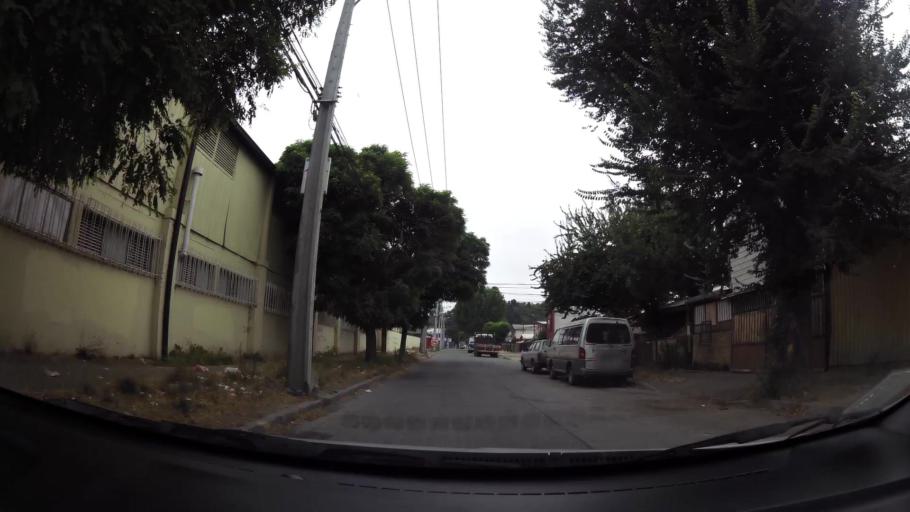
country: CL
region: Biobio
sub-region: Provincia de Concepcion
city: Concepcion
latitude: -36.8150
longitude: -73.0379
